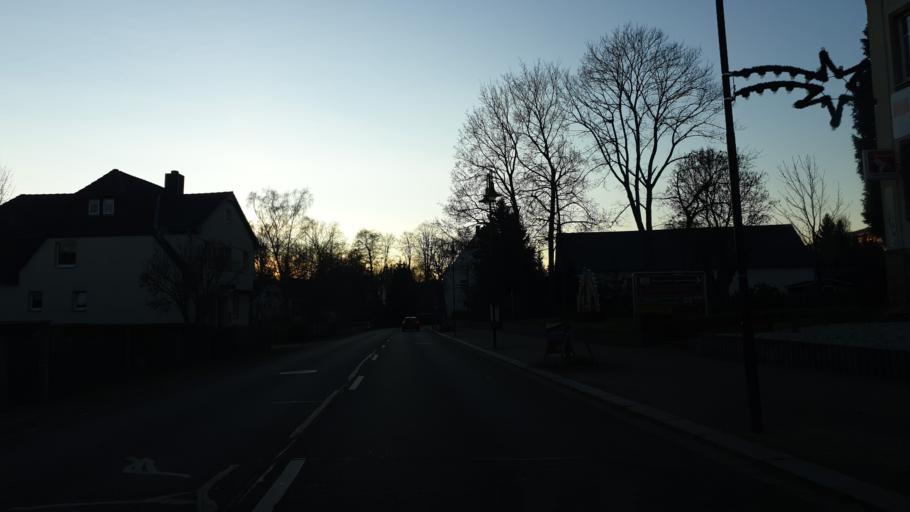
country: DE
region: Saxony
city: Kirchberg
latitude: 50.7898
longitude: 12.7381
